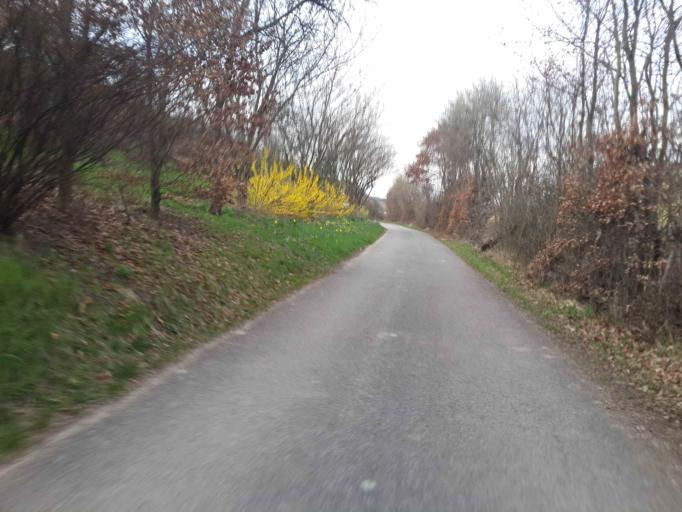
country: DE
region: Baden-Wuerttemberg
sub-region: Regierungsbezirk Stuttgart
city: Boxberg
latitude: 49.4965
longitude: 9.6730
